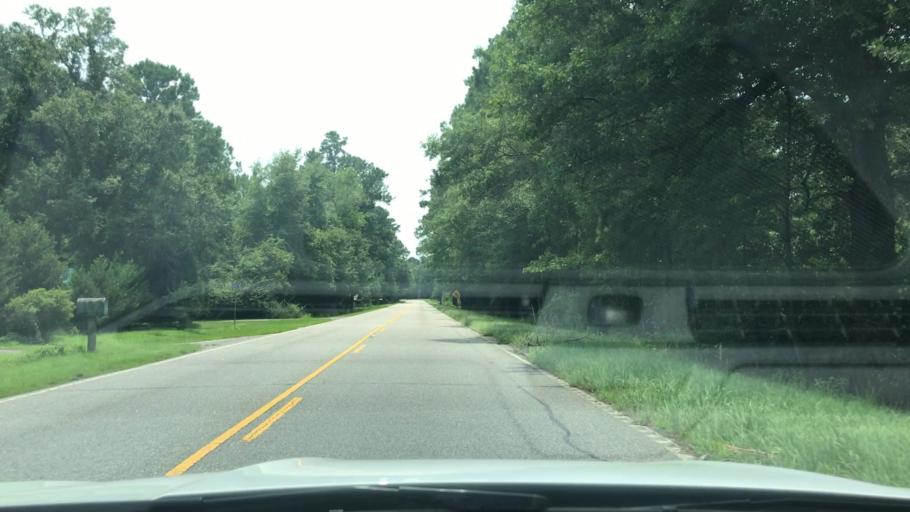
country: US
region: South Carolina
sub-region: Georgetown County
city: Murrells Inlet
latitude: 33.6198
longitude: -79.1936
